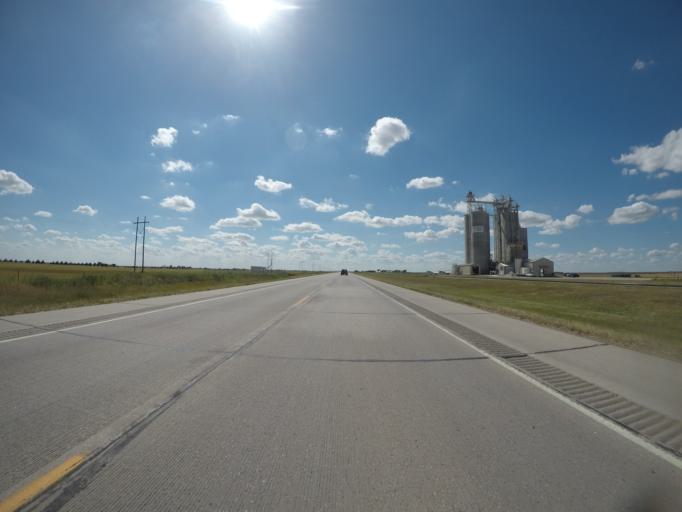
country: US
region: Colorado
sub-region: Phillips County
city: Holyoke
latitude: 40.5909
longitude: -102.3440
